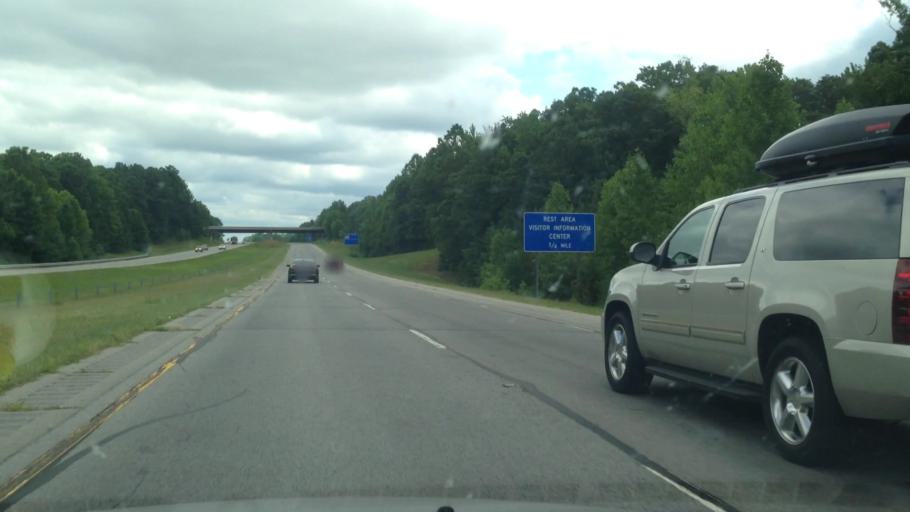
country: US
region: Virginia
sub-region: City of Danville
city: Danville
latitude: 36.5046
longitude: -79.4798
